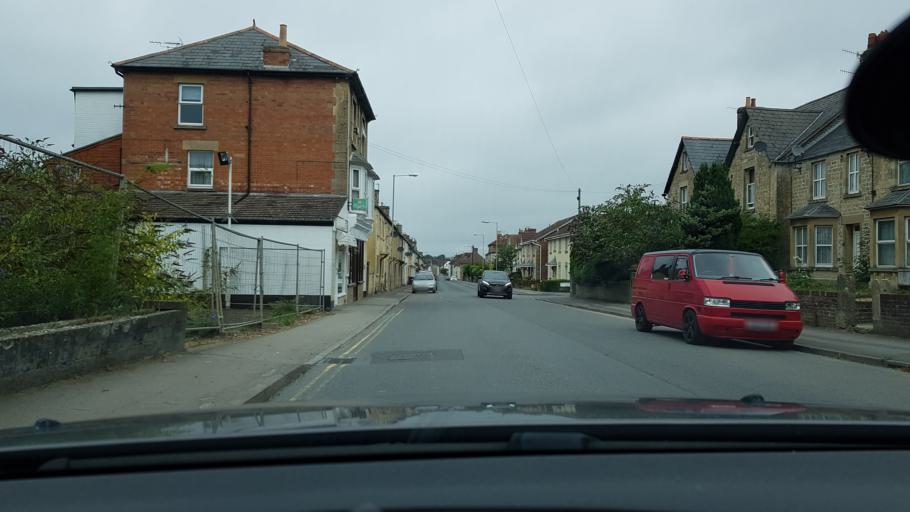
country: GB
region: England
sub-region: Wiltshire
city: Calne
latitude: 51.4316
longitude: -1.9995
